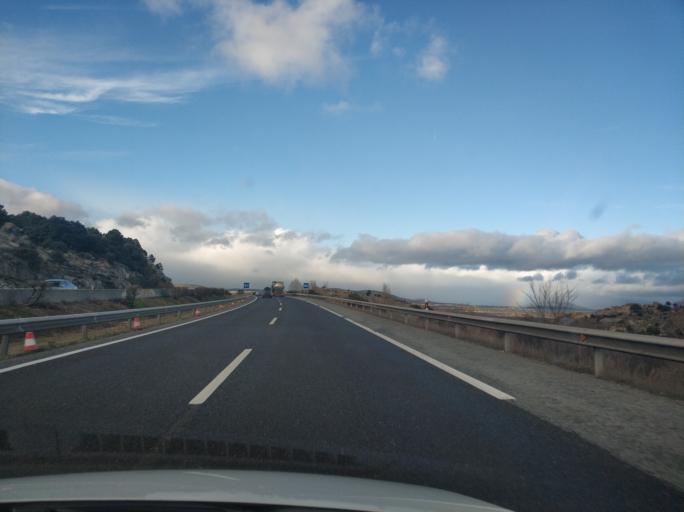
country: ES
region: Madrid
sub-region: Provincia de Madrid
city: La Cabrera
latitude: 40.8871
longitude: -3.5988
